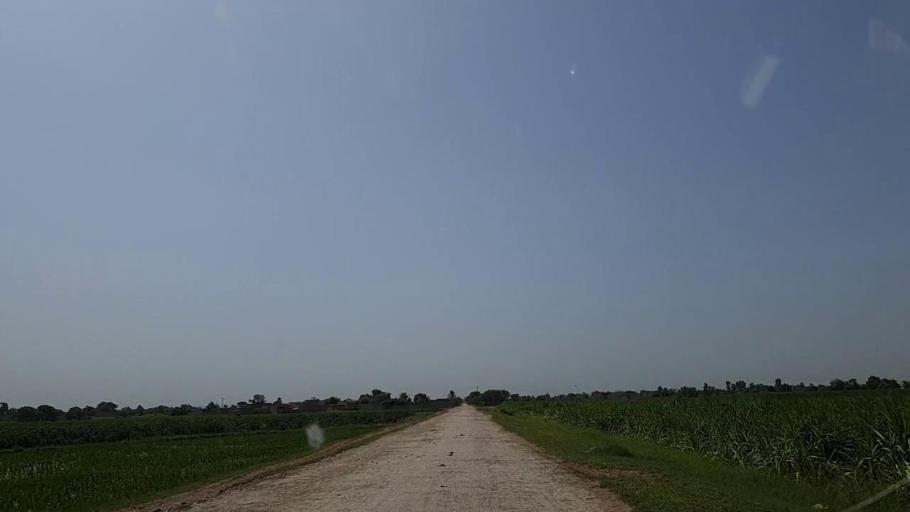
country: PK
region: Sindh
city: Naushahro Firoz
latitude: 26.8525
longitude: 68.0091
